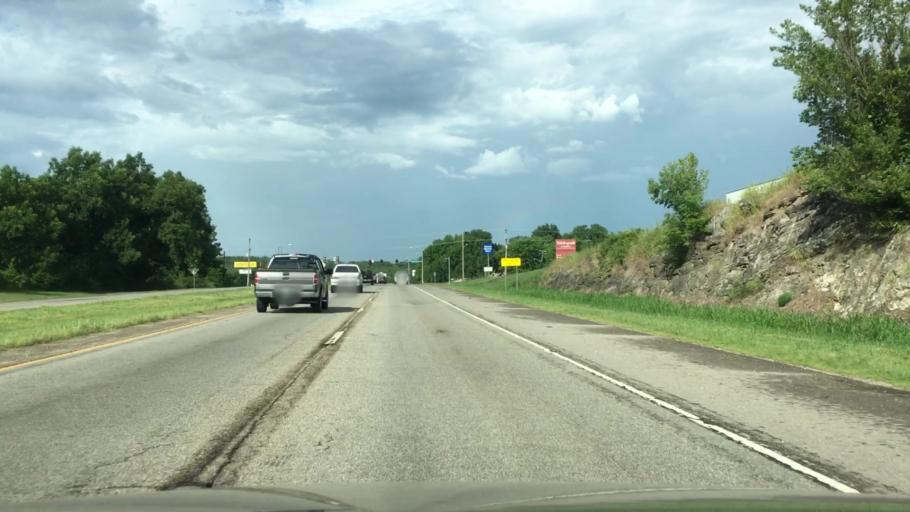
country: US
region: Oklahoma
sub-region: Cherokee County
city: Tahlequah
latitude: 35.8950
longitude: -94.9697
